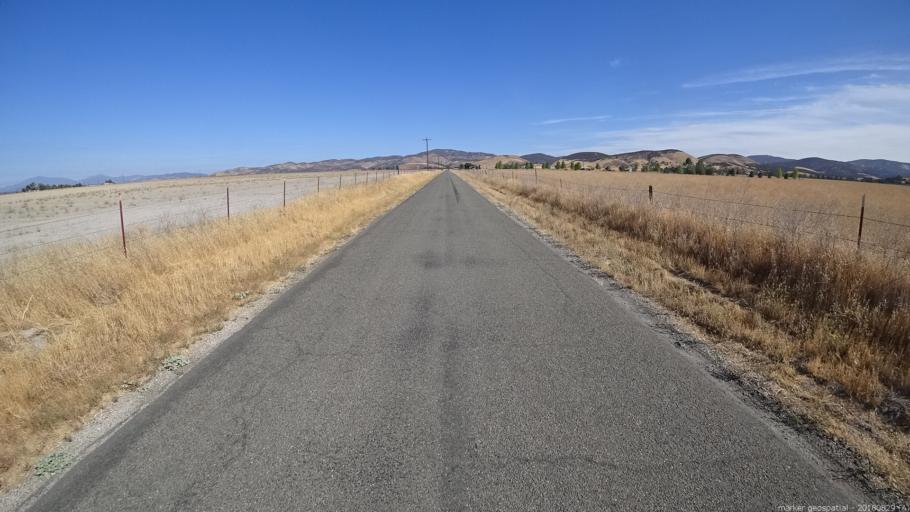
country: US
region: California
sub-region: Monterey County
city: King City
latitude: 35.9480
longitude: -121.0821
